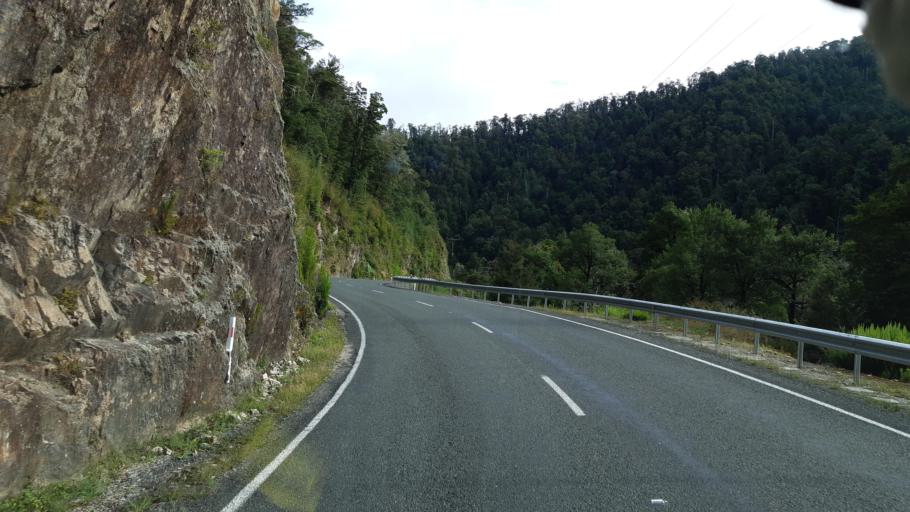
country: NZ
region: West Coast
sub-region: Buller District
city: Westport
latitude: -41.9916
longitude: 172.2196
